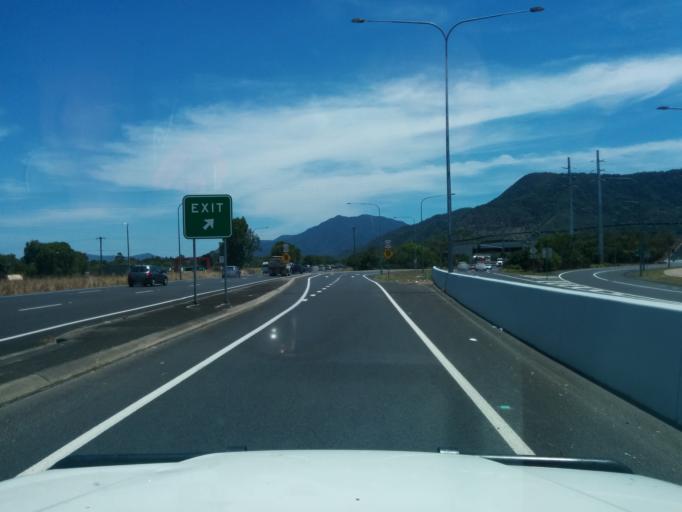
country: AU
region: Queensland
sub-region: Cairns
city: Woree
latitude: -16.9552
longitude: 145.7497
